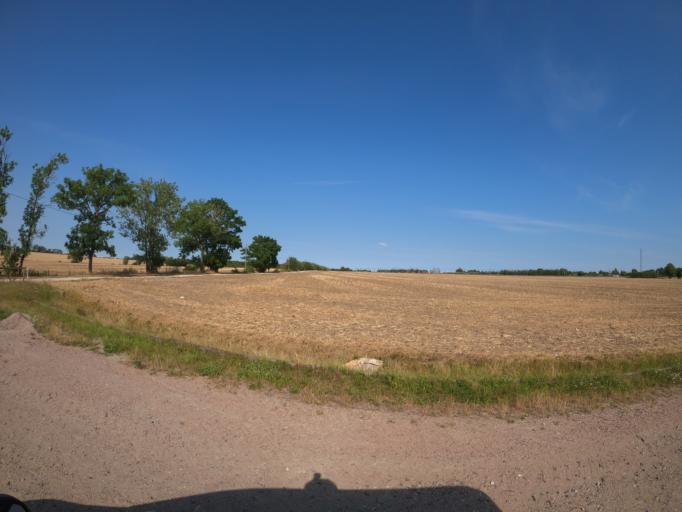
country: SE
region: Skane
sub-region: Lunds Kommun
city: Lund
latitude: 55.7410
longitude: 13.1852
